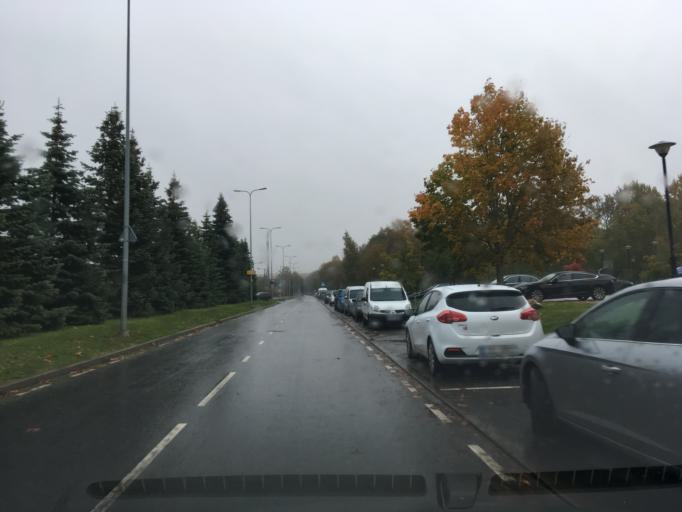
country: EE
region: Harju
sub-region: Tallinna linn
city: Kose
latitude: 59.4549
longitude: 24.8443
